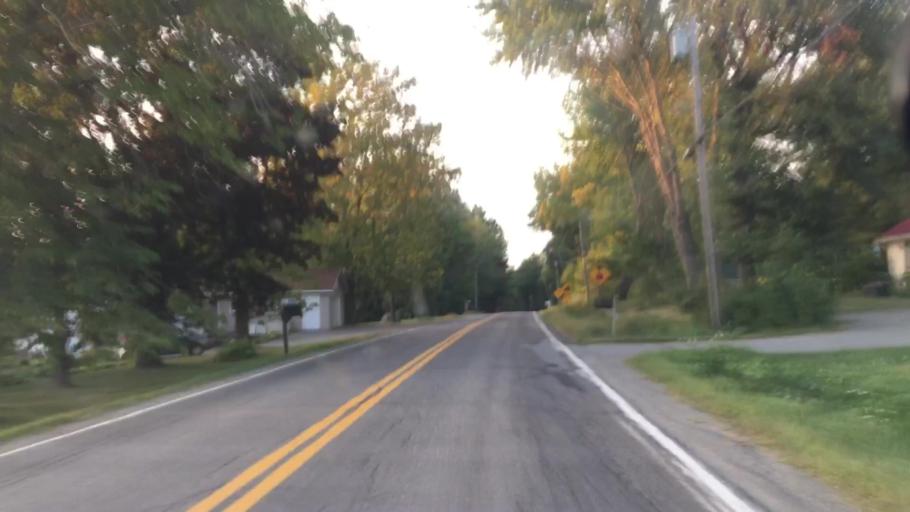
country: US
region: Maine
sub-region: Penobscot County
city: Hermon
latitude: 44.7301
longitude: -68.9617
